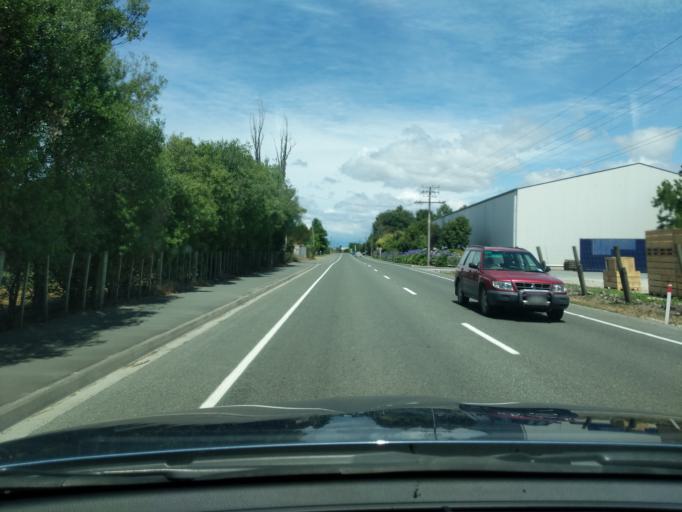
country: NZ
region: Tasman
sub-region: Tasman District
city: Motueka
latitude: -41.0942
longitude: 173.0119
